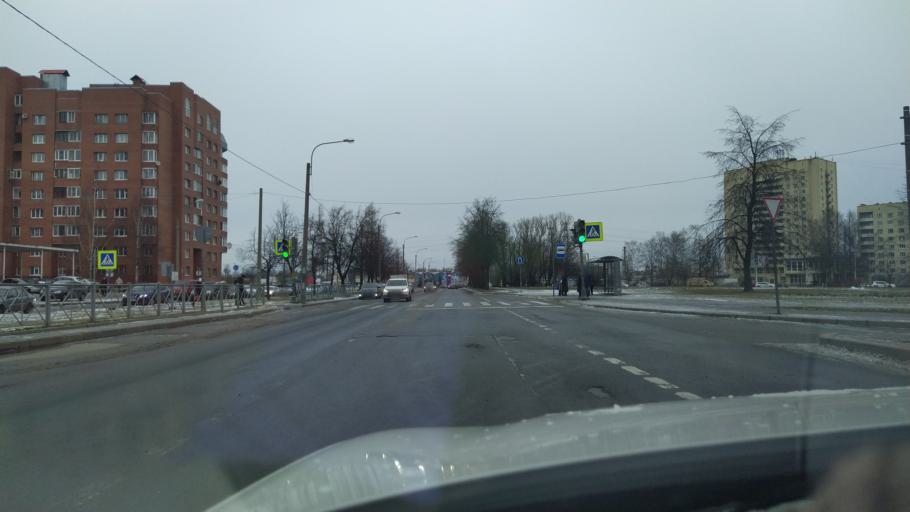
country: RU
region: St.-Petersburg
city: Grazhdanka
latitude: 60.0126
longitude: 30.4301
